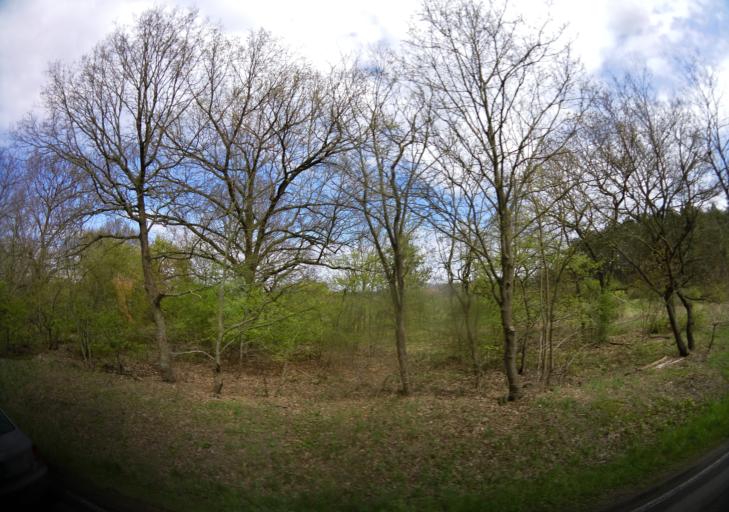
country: DE
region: Brandenburg
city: Potsdam
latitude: 52.3277
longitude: 13.1168
